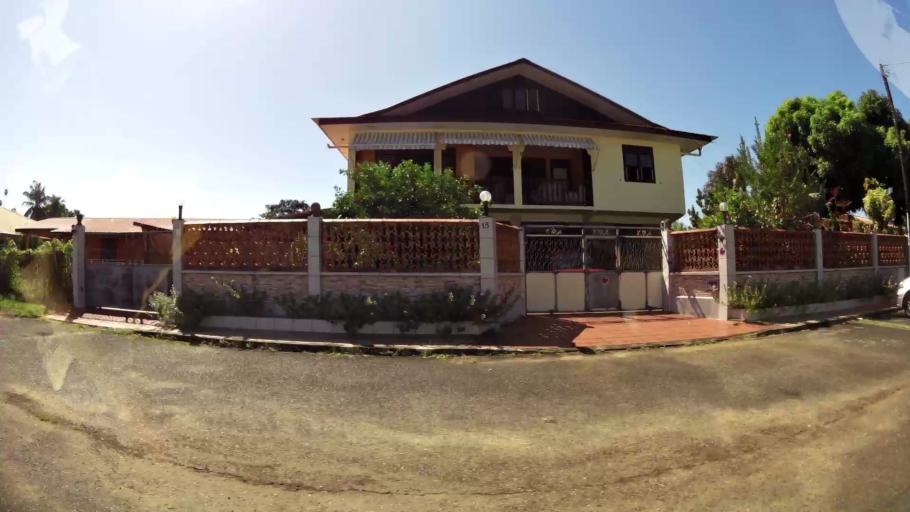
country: GF
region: Guyane
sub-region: Guyane
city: Remire-Montjoly
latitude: 4.9243
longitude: -52.2804
